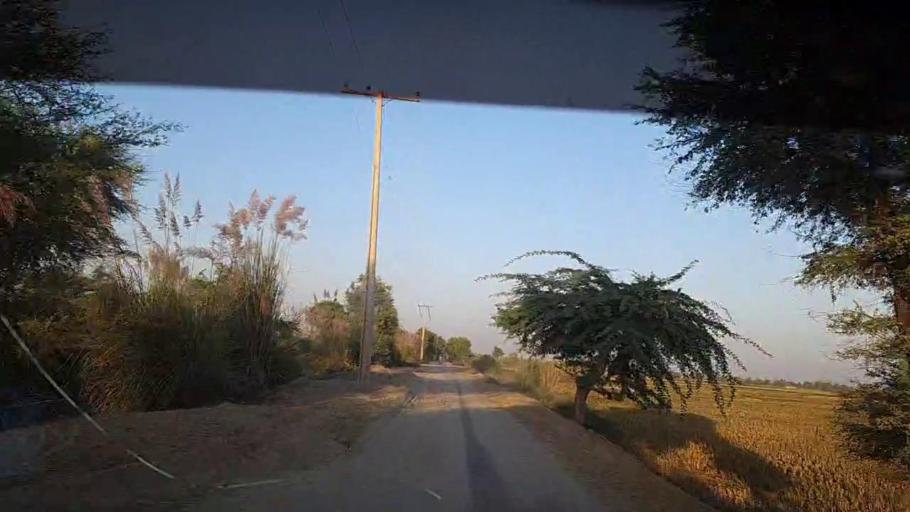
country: PK
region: Sindh
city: Ratodero
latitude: 27.8981
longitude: 68.2301
